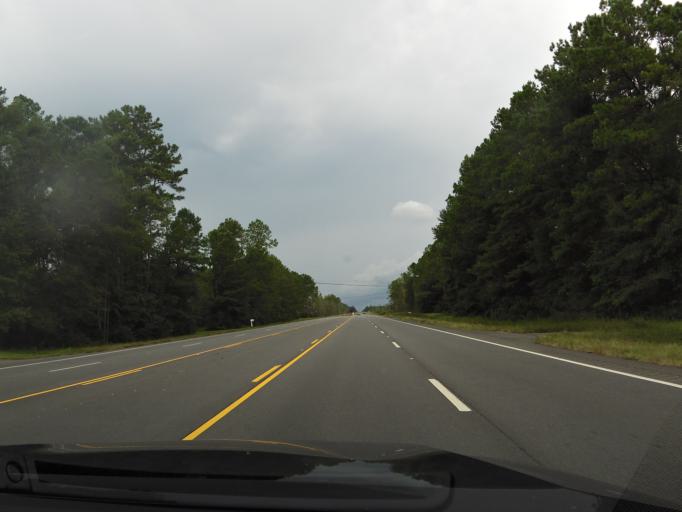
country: US
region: Georgia
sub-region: Glynn County
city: Dock Junction
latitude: 31.3076
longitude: -81.5763
